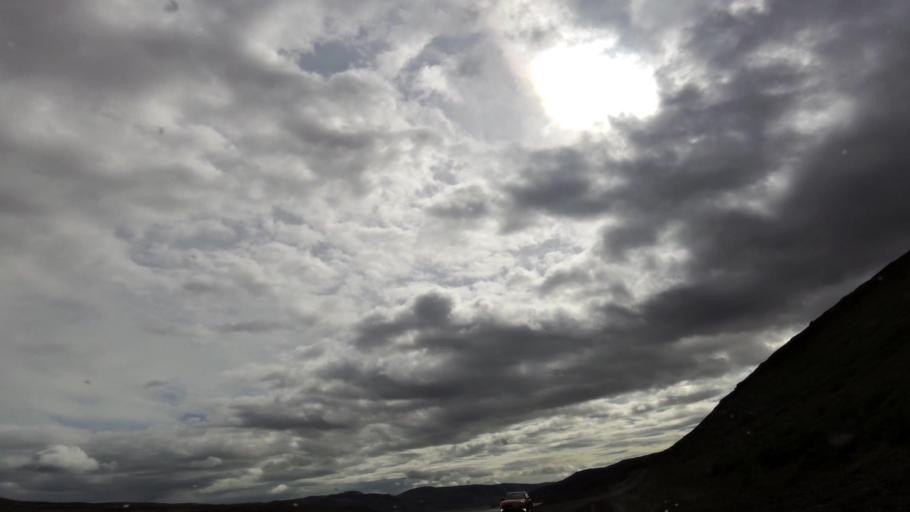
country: IS
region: West
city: Stykkisholmur
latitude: 65.5998
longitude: -22.1144
